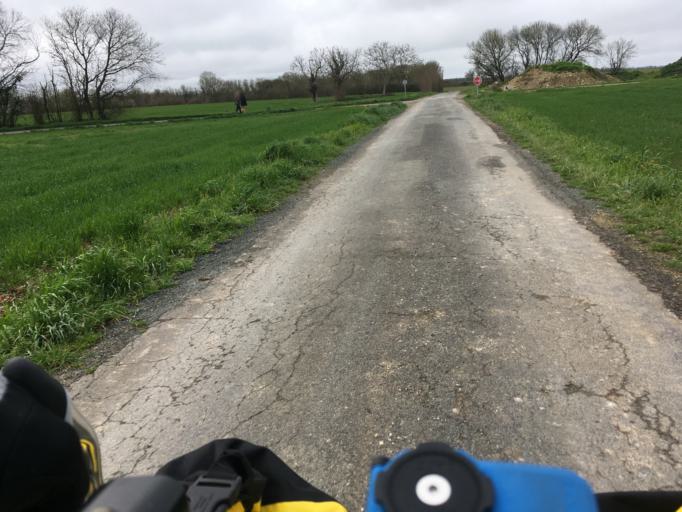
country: FR
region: Poitou-Charentes
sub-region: Departement de la Charente-Maritime
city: Saint-Germain-de-Marencennes
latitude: 46.1173
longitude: -0.8277
